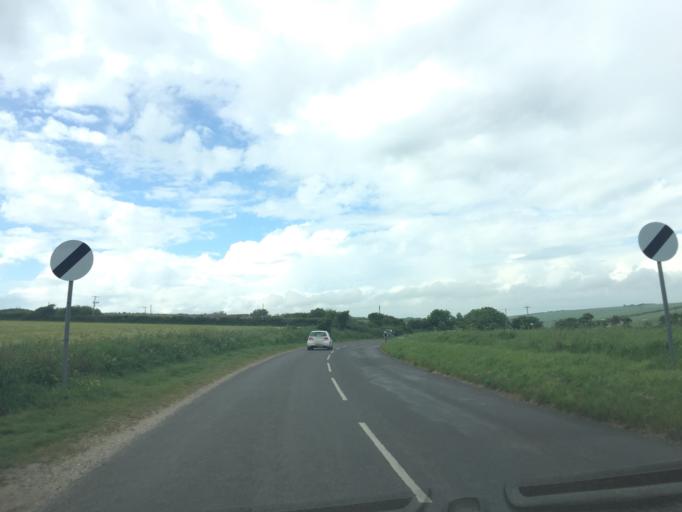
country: GB
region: England
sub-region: Dorset
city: Wool
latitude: 50.6303
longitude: -2.2685
